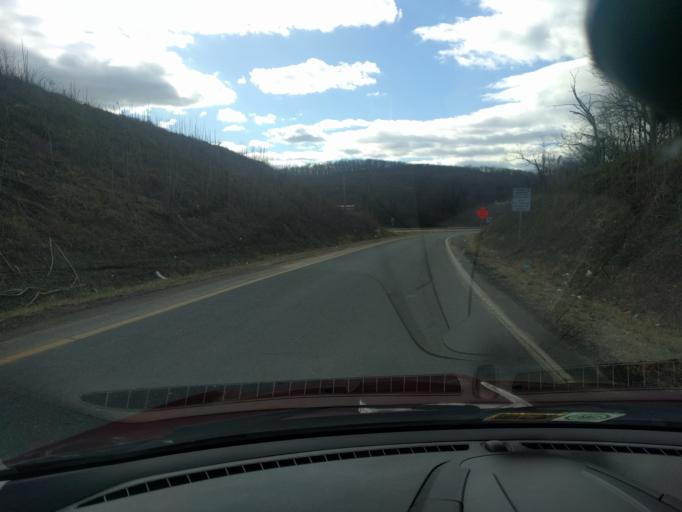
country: US
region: Virginia
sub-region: City of Lynchburg
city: Lynchburg
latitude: 37.3788
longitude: -79.1315
